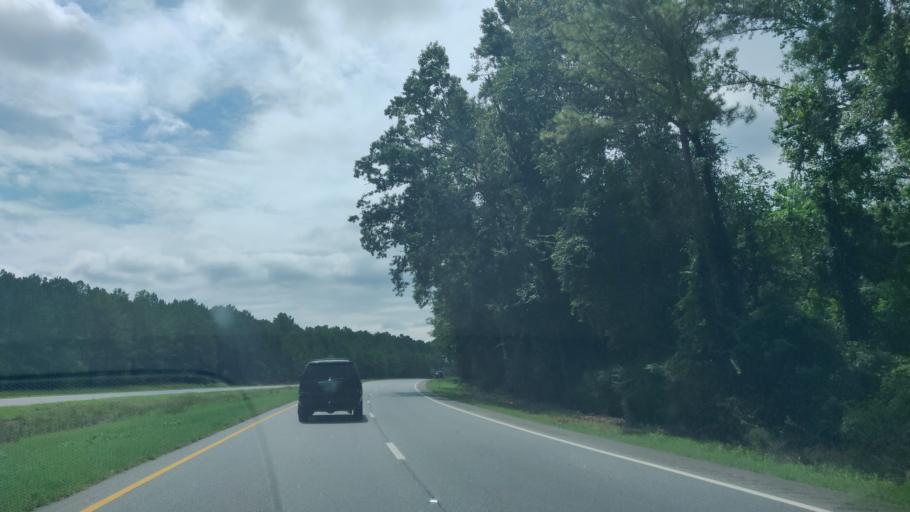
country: US
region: Georgia
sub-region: Terrell County
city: Dawson
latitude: 31.8673
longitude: -84.4857
